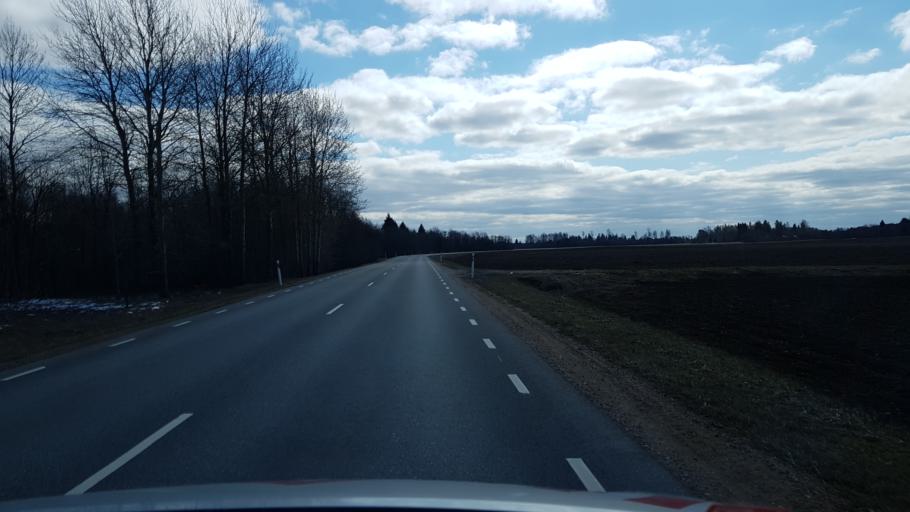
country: EE
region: Laeaene-Virumaa
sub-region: Tapa vald
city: Tapa
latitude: 59.3496
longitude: 26.0042
